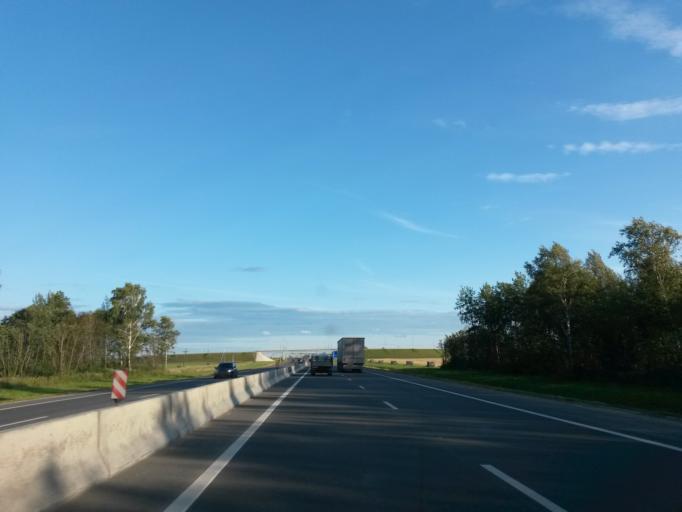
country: RU
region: Jaroslavl
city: Yaroslavl
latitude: 57.7283
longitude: 39.8988
